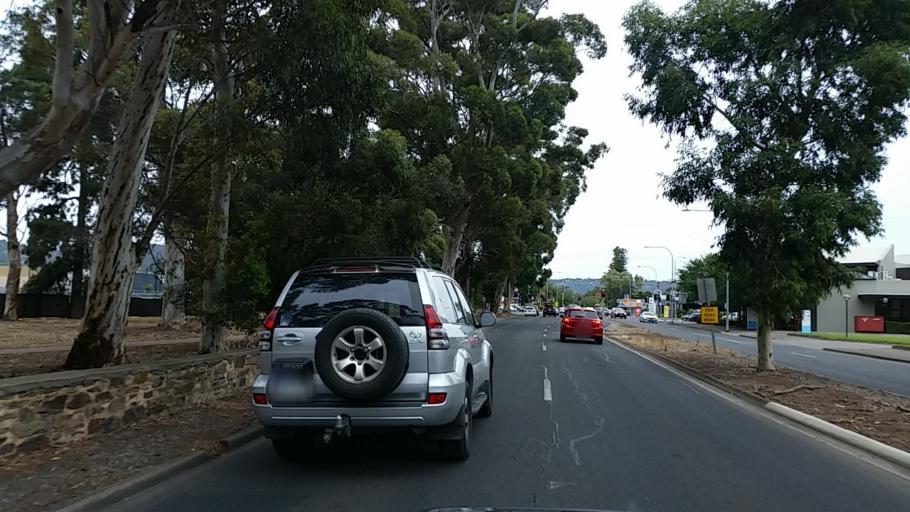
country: AU
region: South Australia
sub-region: Unley
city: Fullarton
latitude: -34.9449
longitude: 138.6250
